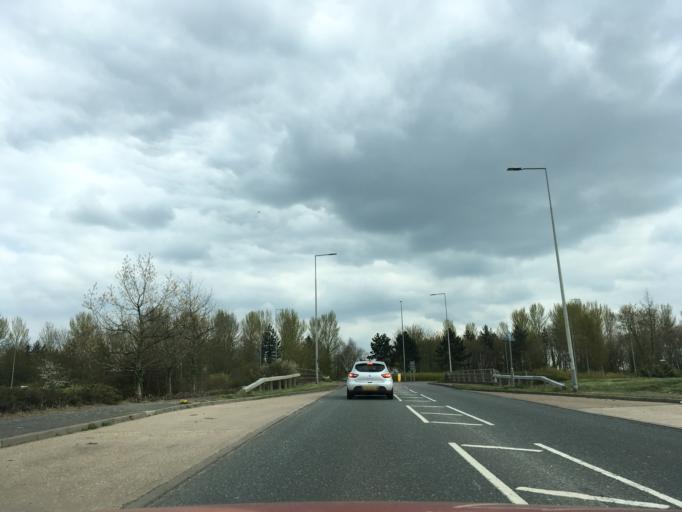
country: GB
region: England
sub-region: Buckinghamshire
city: Newton Longville
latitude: 51.9903
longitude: -0.7862
